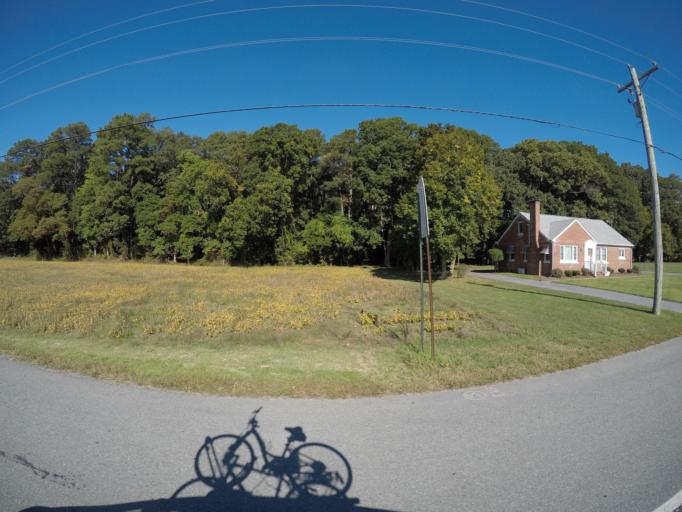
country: US
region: Delaware
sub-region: Sussex County
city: Milton
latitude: 38.8016
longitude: -75.2793
